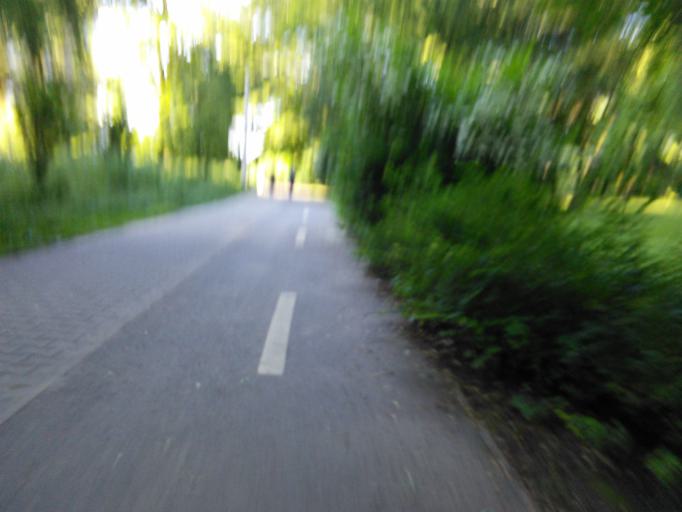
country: PL
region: Silesian Voivodeship
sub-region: Bytom
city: Bytom
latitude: 50.3521
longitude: 18.9004
